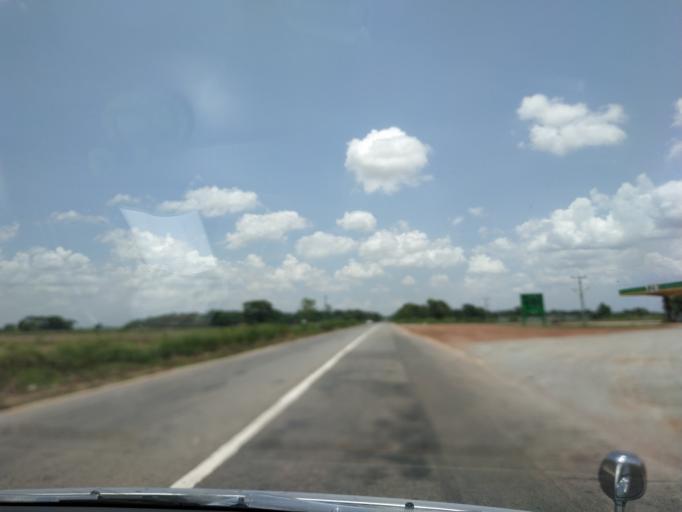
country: MM
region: Bago
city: Thanatpin
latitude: 17.4518
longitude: 96.6169
